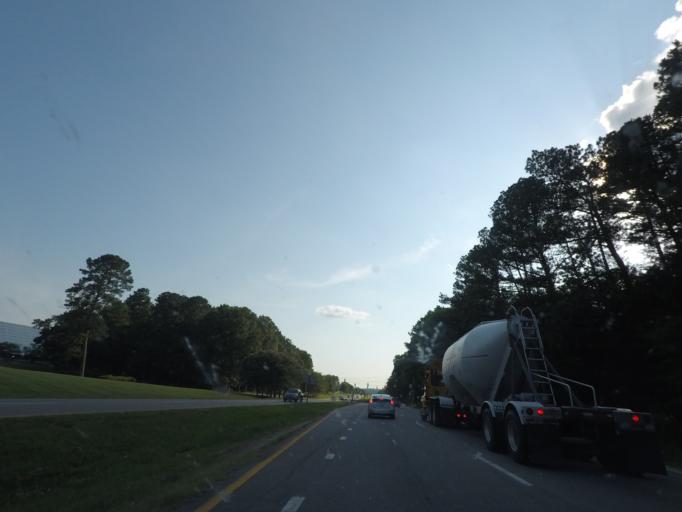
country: US
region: North Carolina
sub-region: Orange County
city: Chapel Hill
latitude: 35.9478
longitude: -79.0060
